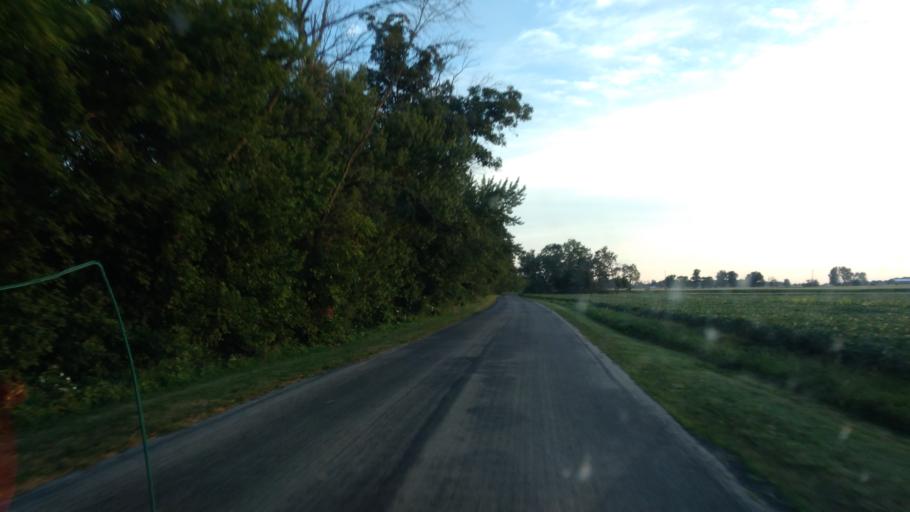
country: US
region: Indiana
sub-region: Adams County
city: Berne
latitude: 40.6508
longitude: -85.0312
